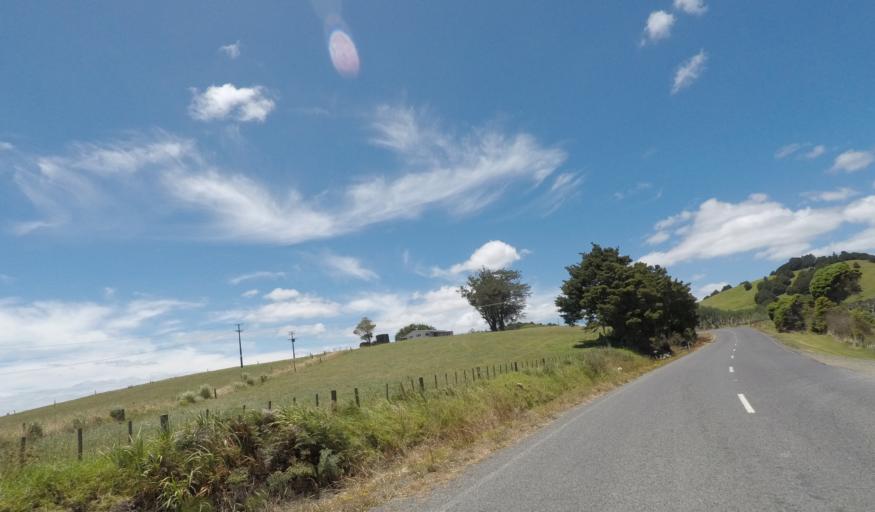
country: NZ
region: Northland
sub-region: Whangarei
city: Whangarei
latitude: -35.5597
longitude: 174.2884
